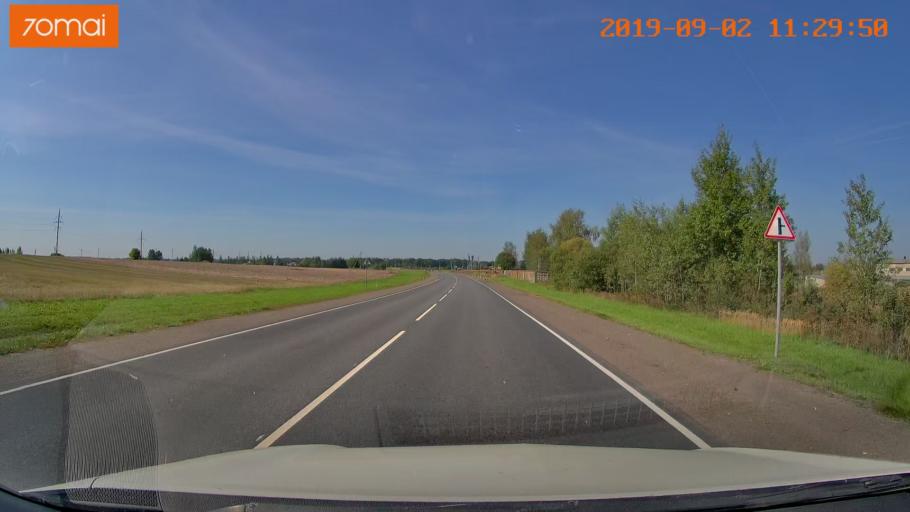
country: RU
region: Smolensk
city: Roslavl'
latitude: 53.9881
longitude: 32.8497
